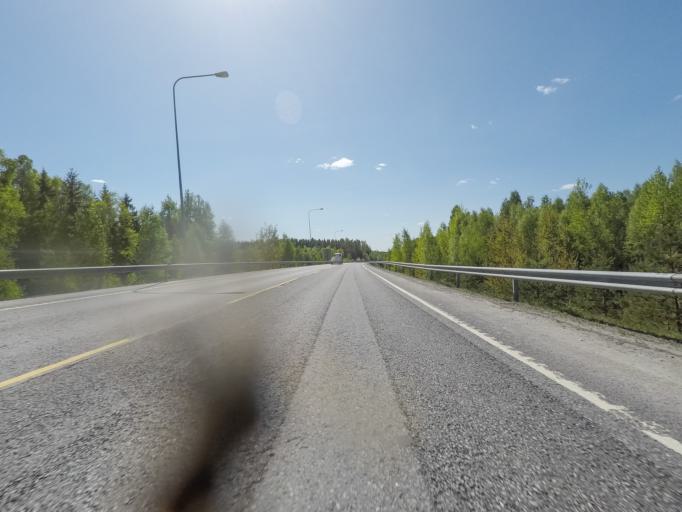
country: FI
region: Pirkanmaa
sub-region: Etelae-Pirkanmaa
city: Toijala
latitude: 61.1889
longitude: 23.8065
